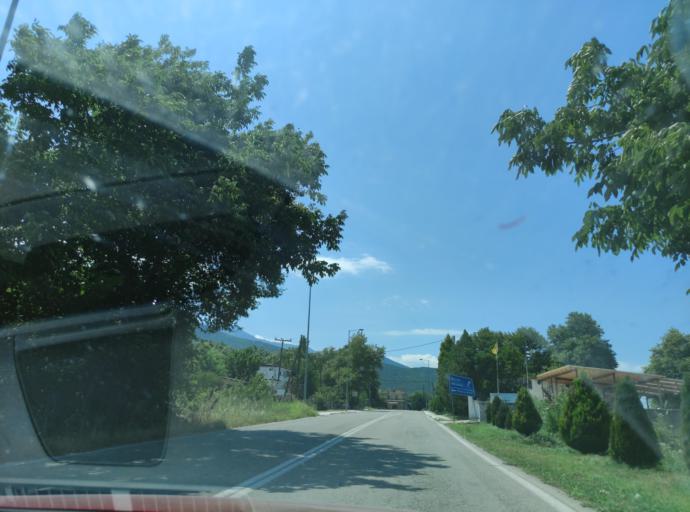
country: GR
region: East Macedonia and Thrace
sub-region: Nomos Kavalas
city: Palaiochori
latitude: 40.9528
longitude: 24.1963
